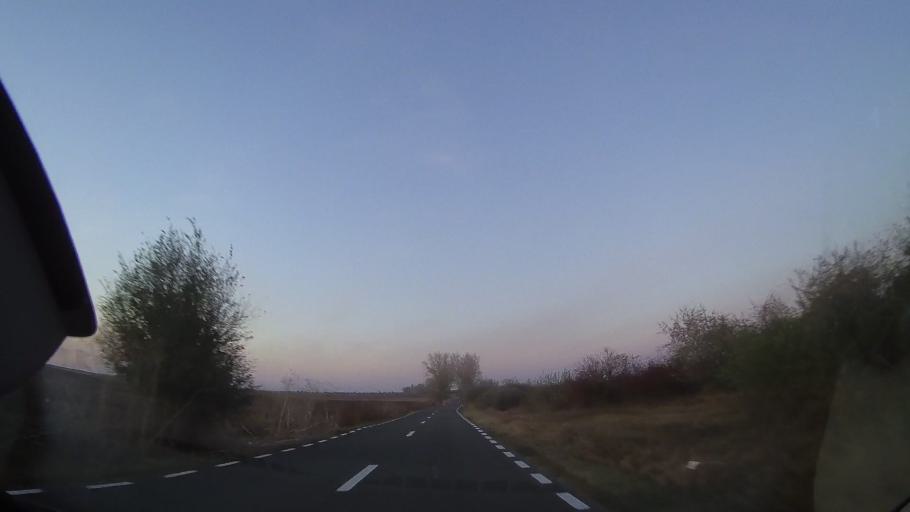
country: RO
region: Constanta
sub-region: Comuna Cobadin
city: Cobadin
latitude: 44.0369
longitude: 28.2588
